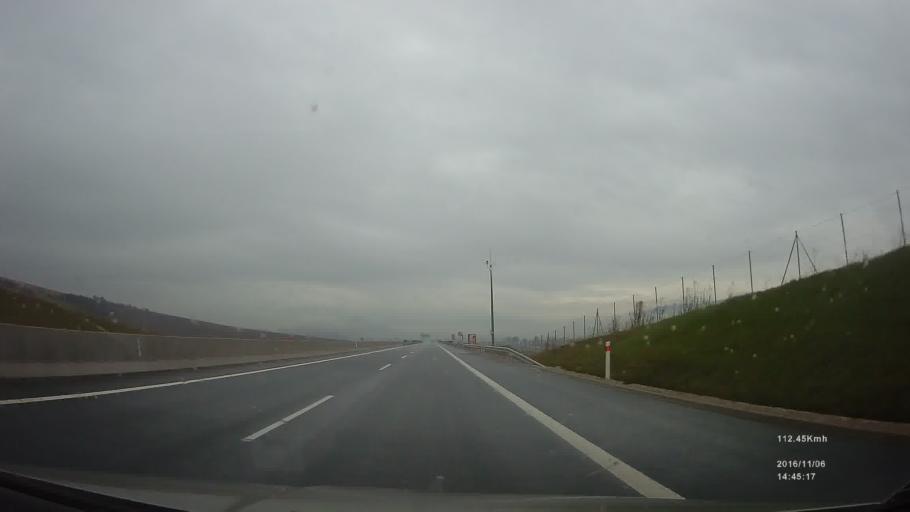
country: SK
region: Presovsky
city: Spisske Podhradie
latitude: 49.0086
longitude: 20.6732
